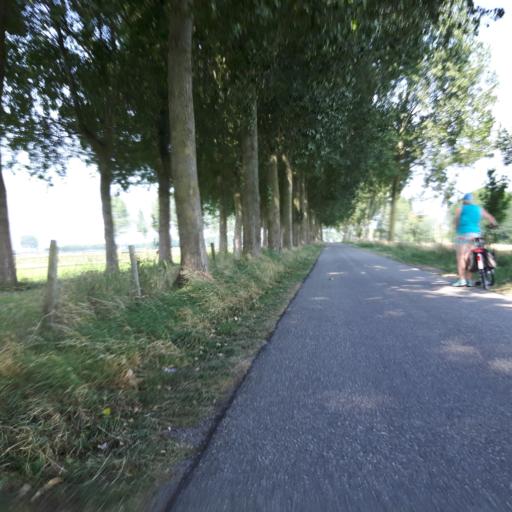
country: NL
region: Zeeland
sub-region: Gemeente Goes
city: Goes
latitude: 51.4524
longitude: 3.9256
